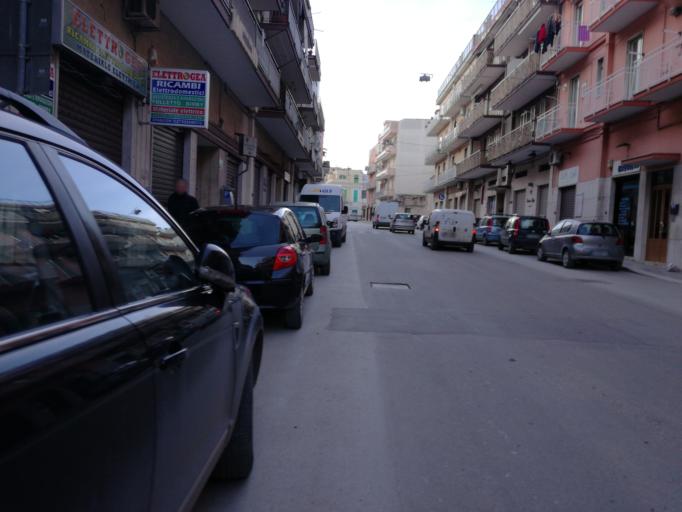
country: IT
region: Apulia
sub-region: Provincia di Bari
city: Corato
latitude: 41.1483
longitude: 16.4143
